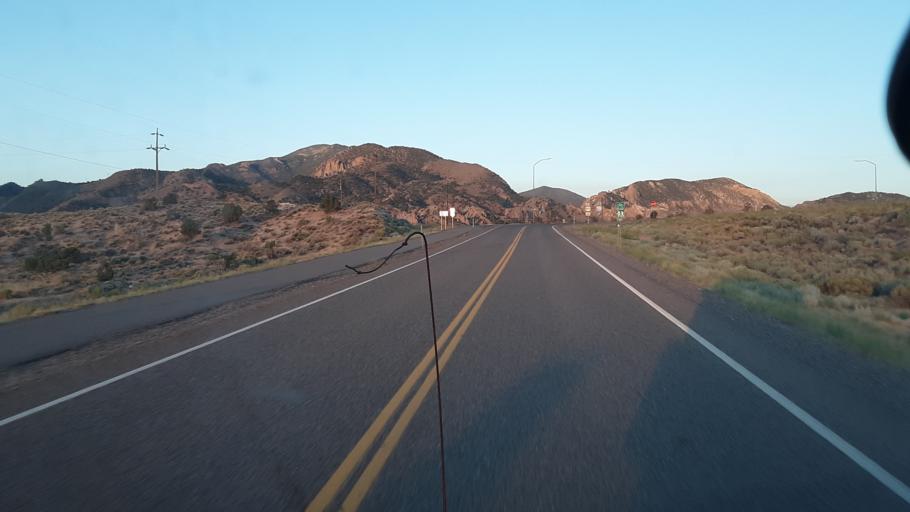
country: US
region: Utah
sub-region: Sevier County
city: Monroe
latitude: 38.5902
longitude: -112.2566
